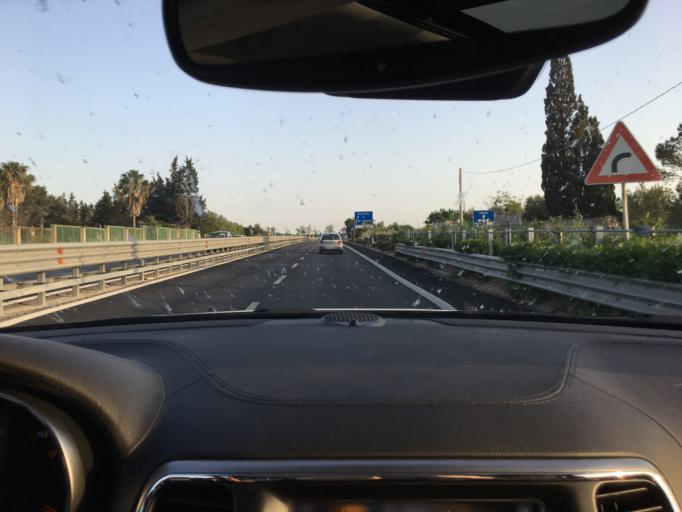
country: IT
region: Apulia
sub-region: Provincia di Lecce
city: San Pietro in Lama
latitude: 40.2936
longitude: 18.1326
